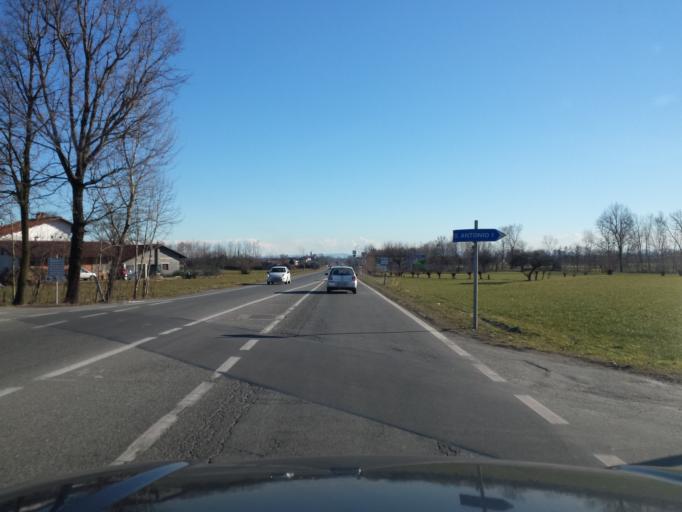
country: IT
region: Piedmont
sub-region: Provincia di Torino
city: Castellamonte
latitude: 45.3644
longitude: 7.7255
